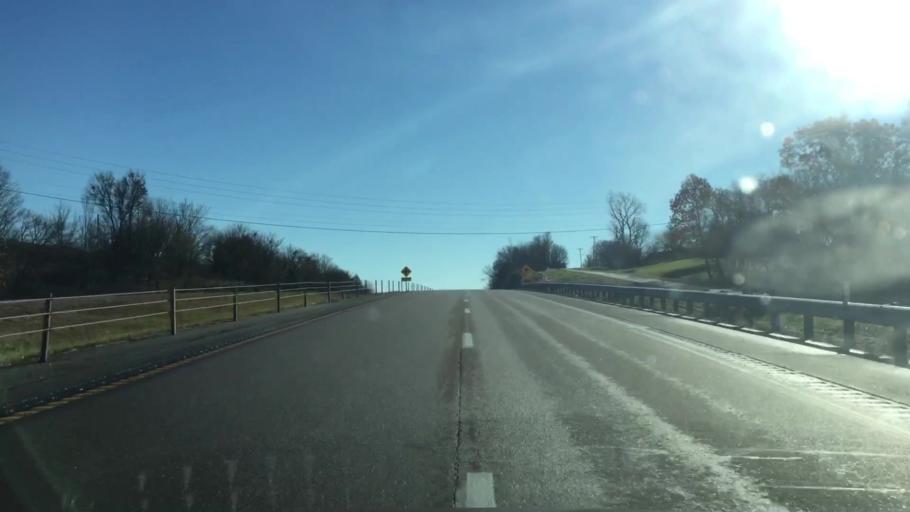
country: US
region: Missouri
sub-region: Boone County
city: Ashland
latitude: 38.6748
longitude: -92.2429
